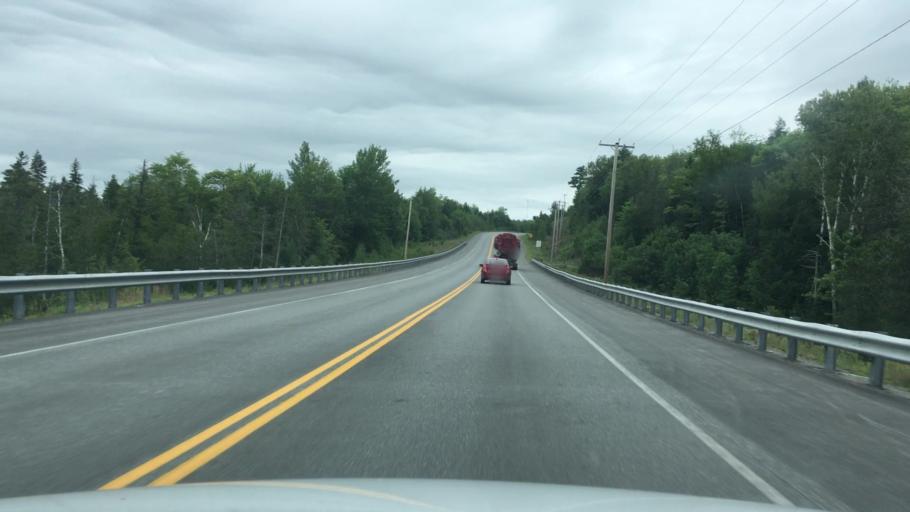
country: US
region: Maine
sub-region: Hancock County
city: Franklin
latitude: 44.8417
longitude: -68.3442
